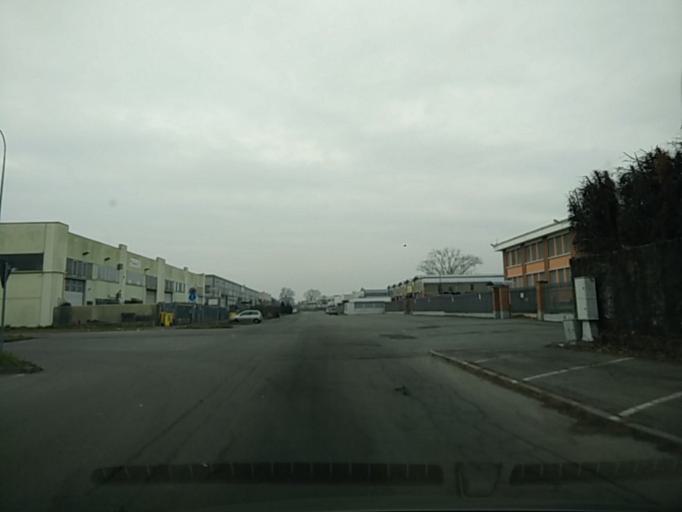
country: IT
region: Piedmont
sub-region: Provincia di Torino
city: Leini
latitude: 45.1488
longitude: 7.7265
